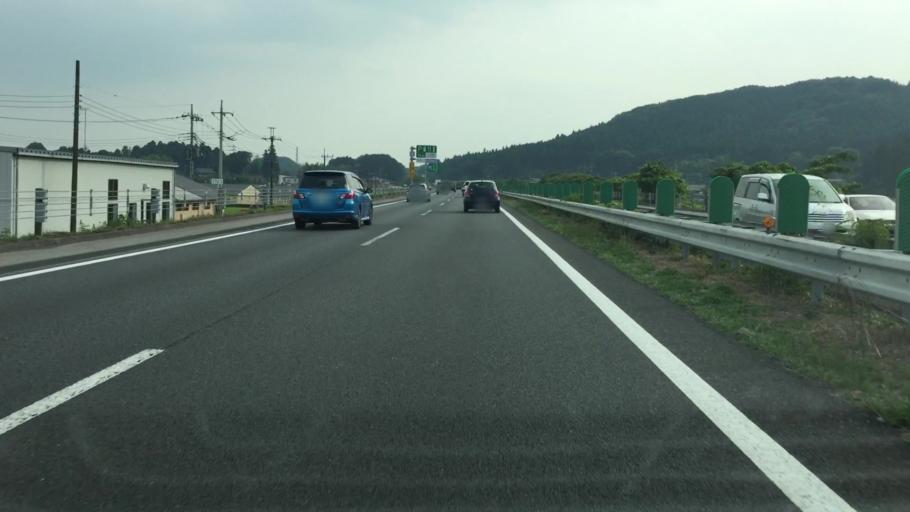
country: JP
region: Tochigi
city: Ujiie
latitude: 36.7020
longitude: 139.8989
